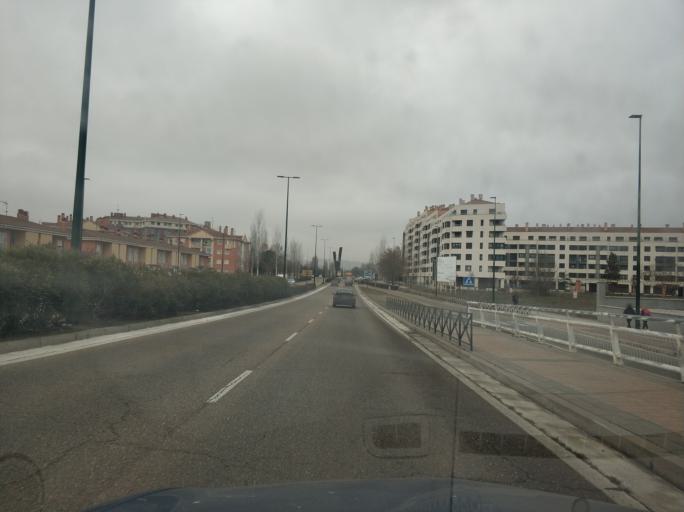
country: ES
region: Castille and Leon
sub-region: Provincia de Valladolid
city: Valladolid
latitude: 41.6219
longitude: -4.7441
